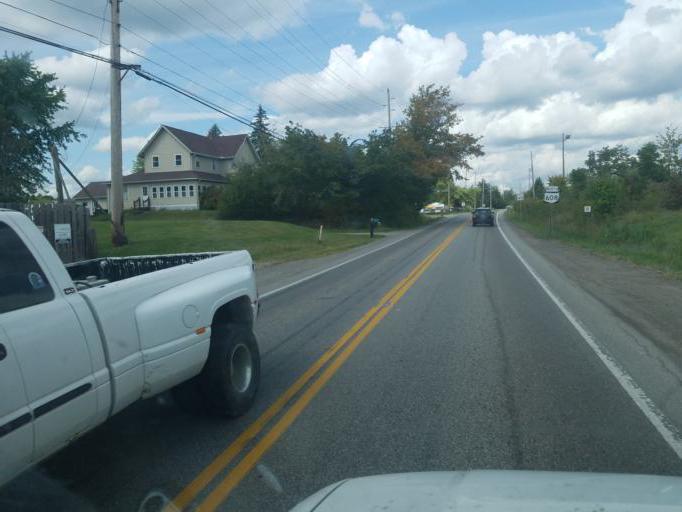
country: US
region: Ohio
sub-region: Geauga County
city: Middlefield
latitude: 41.4367
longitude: -81.0585
